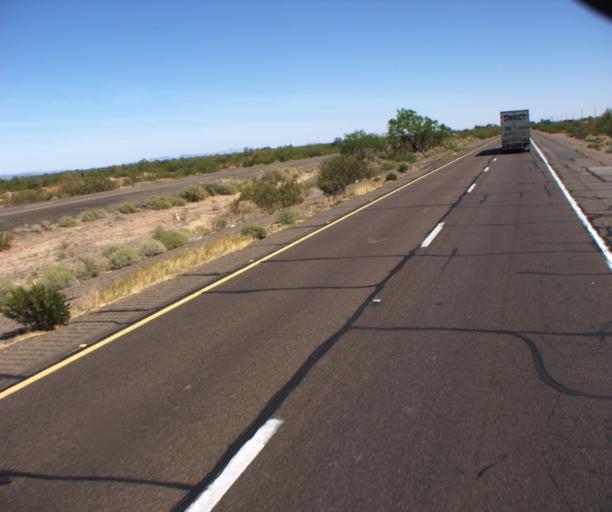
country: US
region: Arizona
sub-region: Yuma County
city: Wellton
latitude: 32.8211
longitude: -113.4683
